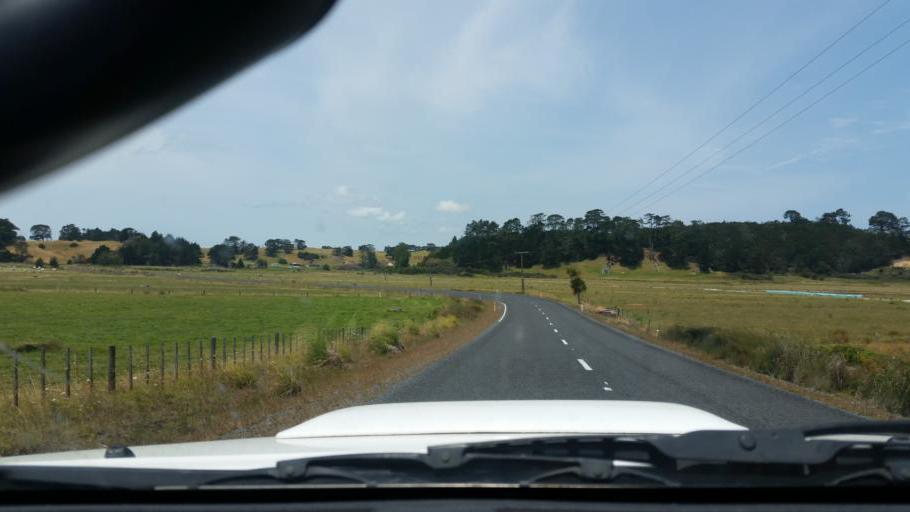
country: NZ
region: Northland
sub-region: Kaipara District
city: Dargaville
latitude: -36.1898
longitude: 174.0349
